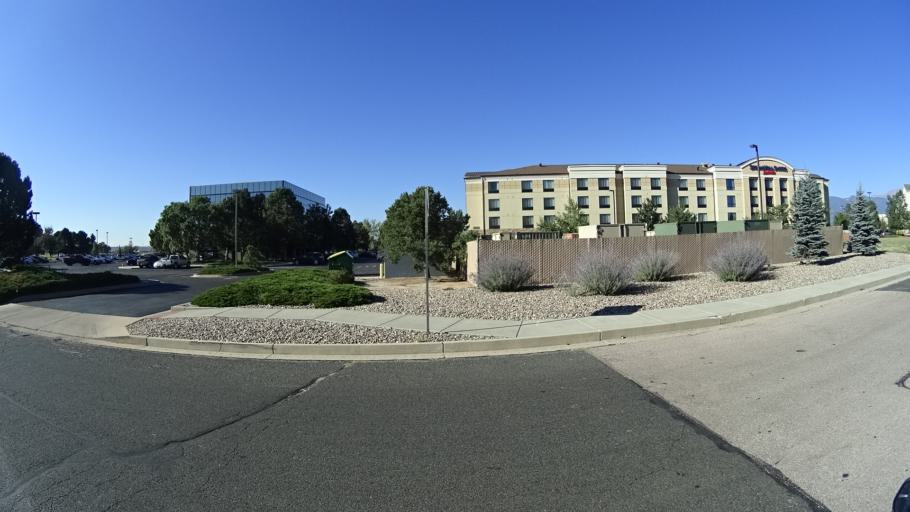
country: US
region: Colorado
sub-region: El Paso County
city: Cimarron Hills
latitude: 38.8082
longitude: -104.7274
